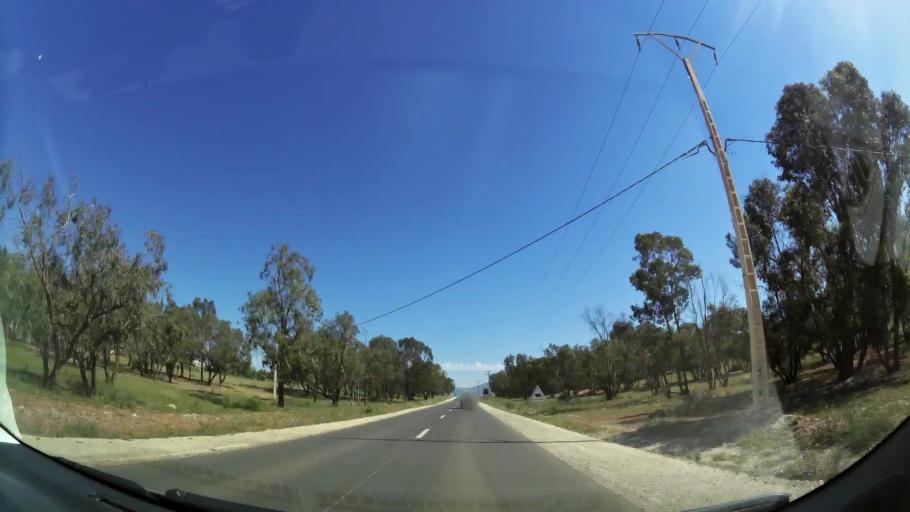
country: MA
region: Oriental
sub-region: Berkane-Taourirt
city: Madagh
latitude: 34.9992
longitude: -2.3948
